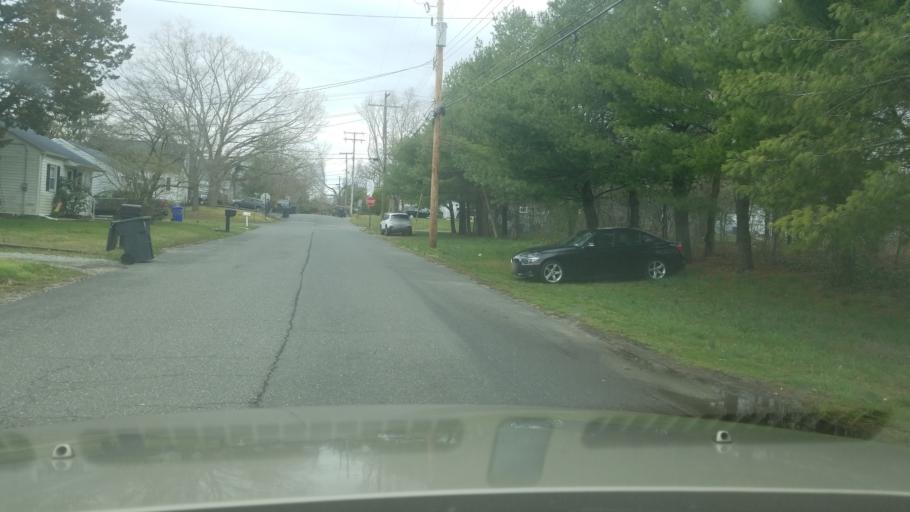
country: US
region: New Jersey
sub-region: Ocean County
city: Toms River
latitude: 39.9645
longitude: -74.1892
